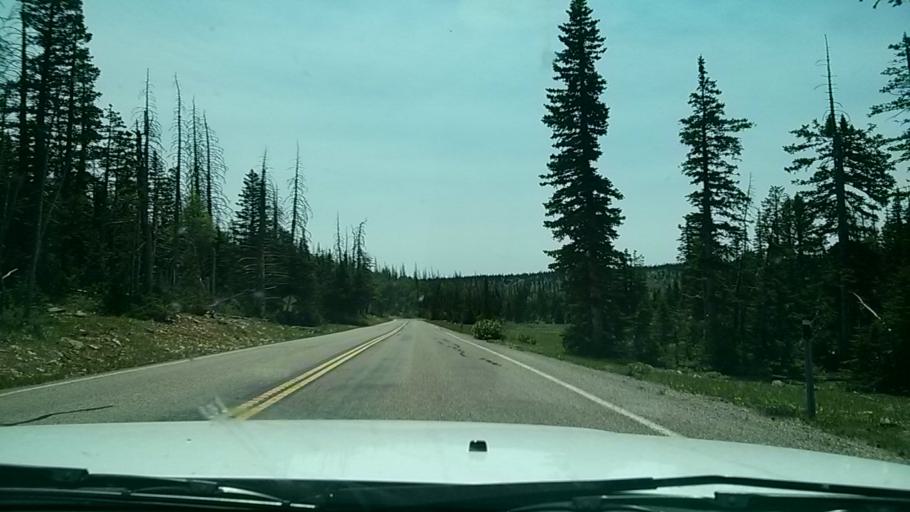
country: US
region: Utah
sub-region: Iron County
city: Cedar City
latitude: 37.5823
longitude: -112.8452
